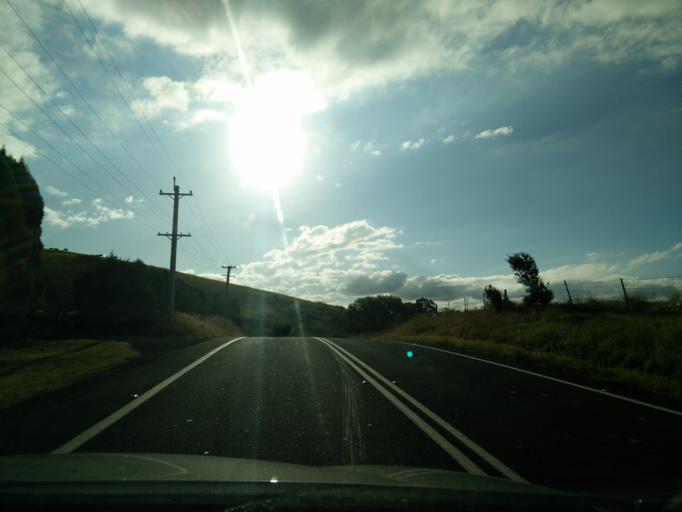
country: AU
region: New South Wales
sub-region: Shellharbour
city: Albion Park Rail
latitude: -34.6034
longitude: 150.7833
